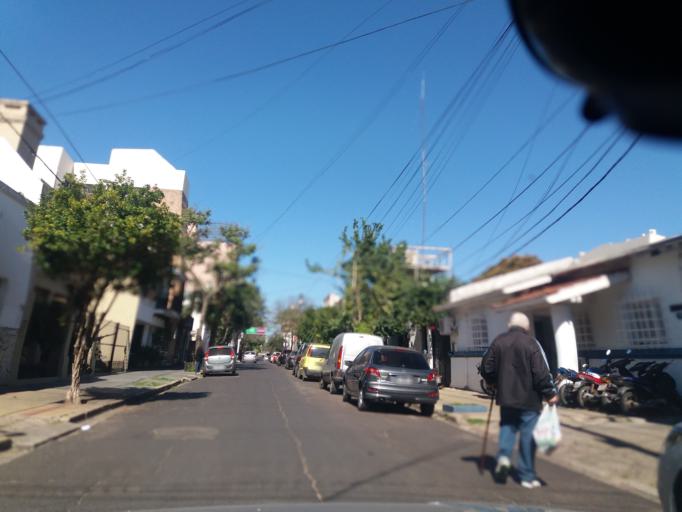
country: AR
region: Corrientes
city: Corrientes
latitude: -27.4716
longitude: -58.8445
